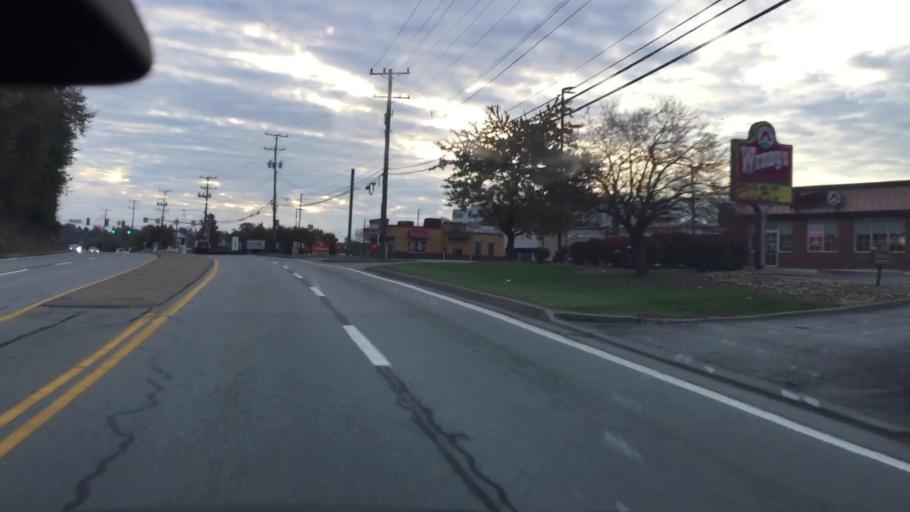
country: US
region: Pennsylvania
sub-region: Allegheny County
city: Turtle Creek
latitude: 40.4306
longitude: -79.8143
